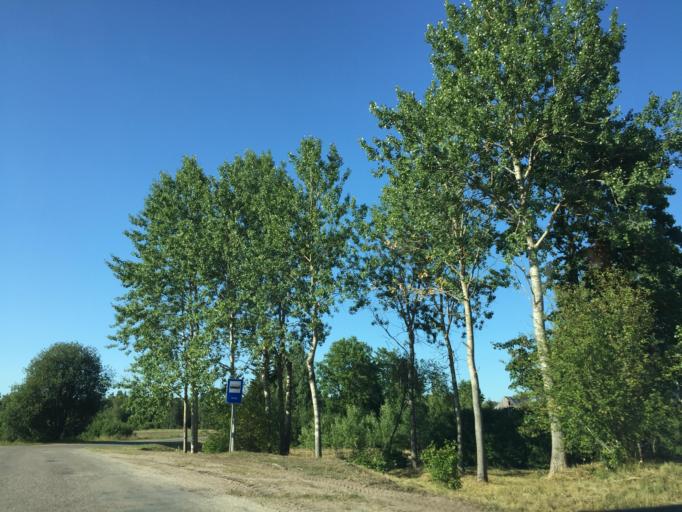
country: LV
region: Talsu Rajons
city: Sabile
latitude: 57.1337
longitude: 22.6502
